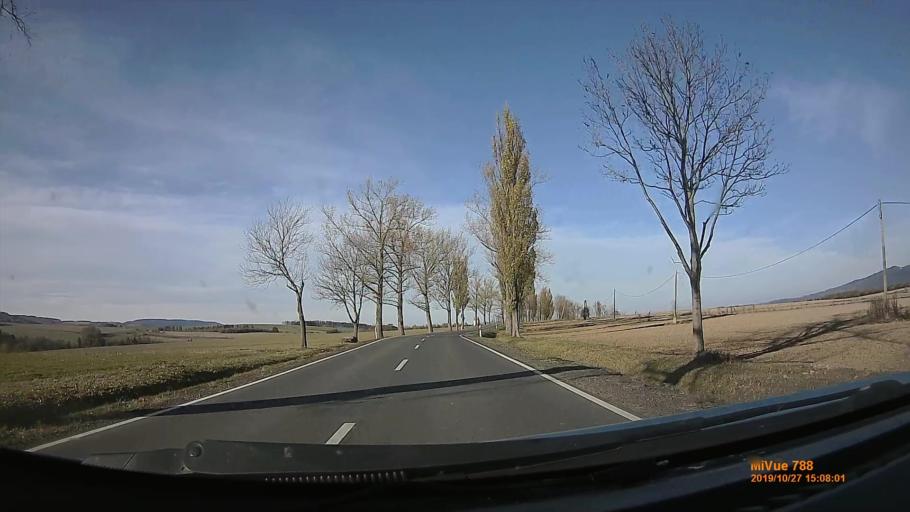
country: PL
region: Lower Silesian Voivodeship
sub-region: Powiat klodzki
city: Miedzylesie
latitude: 50.1646
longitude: 16.6688
